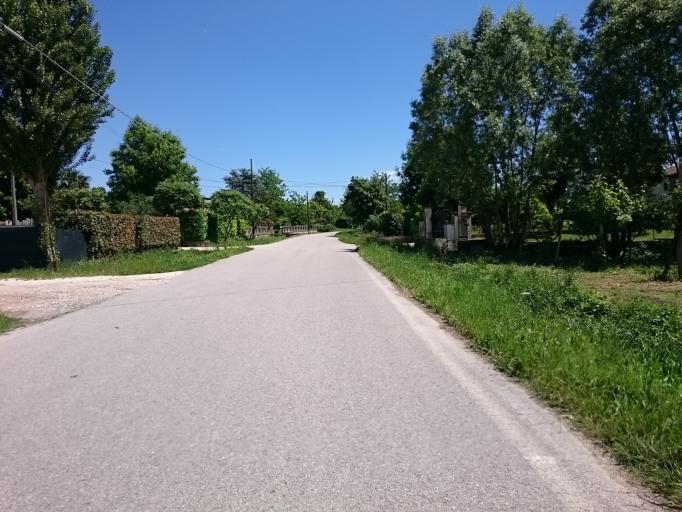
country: IT
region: Veneto
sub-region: Provincia di Padova
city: Campagnola
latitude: 45.2695
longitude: 11.9996
